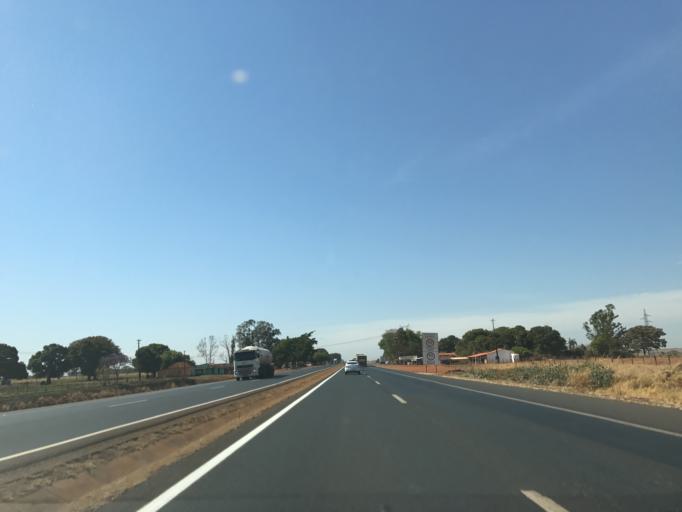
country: BR
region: Minas Gerais
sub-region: Centralina
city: Centralina
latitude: -18.7212
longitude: -49.1233
